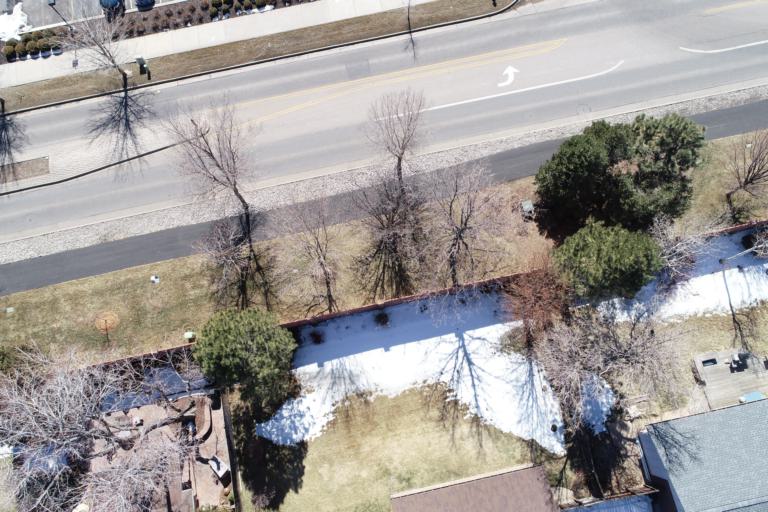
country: US
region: Colorado
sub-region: Arapahoe County
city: Centennial
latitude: 39.6244
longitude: -104.8780
